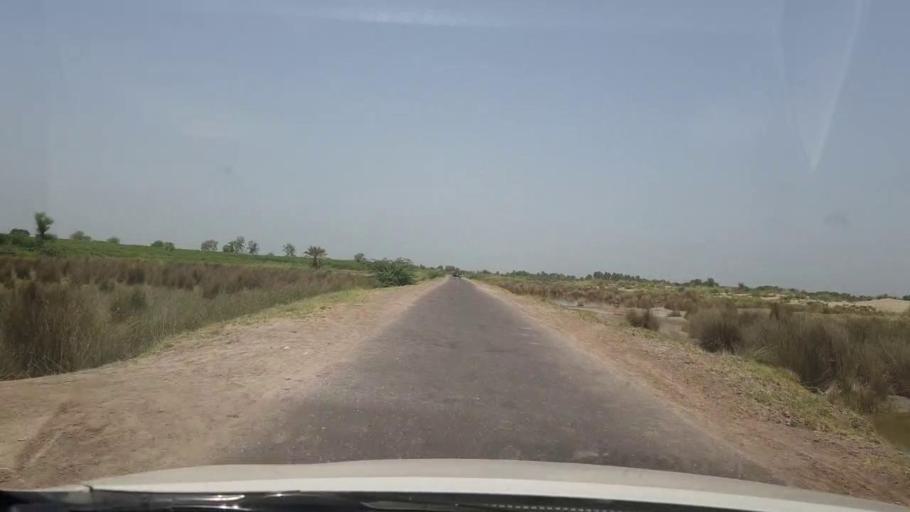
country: PK
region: Sindh
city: Bozdar
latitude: 27.2522
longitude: 68.6409
